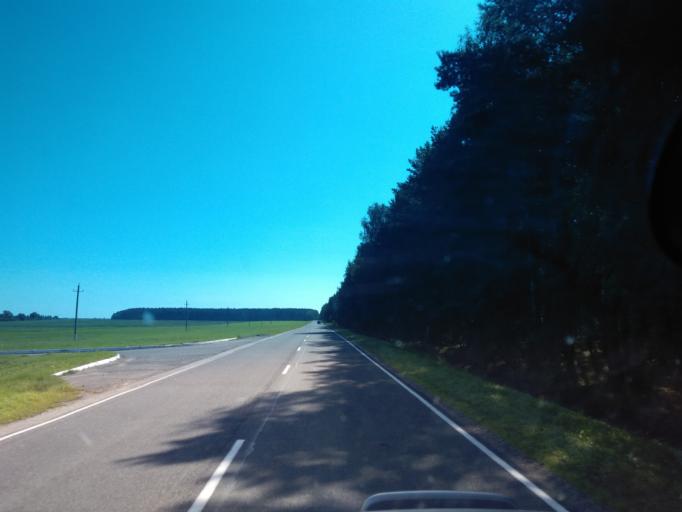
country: BY
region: Minsk
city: Stan'kava
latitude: 53.6249
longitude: 27.2762
